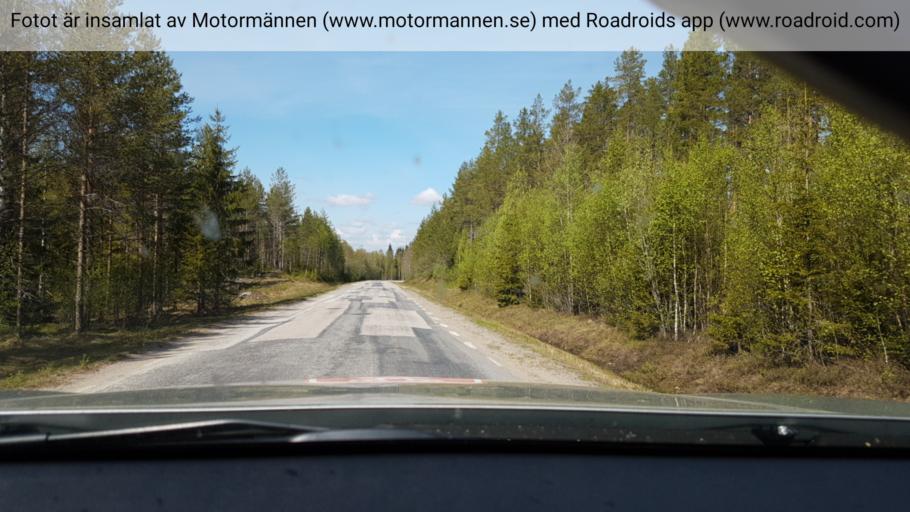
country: SE
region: Vaesterbotten
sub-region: Umea Kommun
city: Saevar
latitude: 63.8467
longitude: 20.5955
